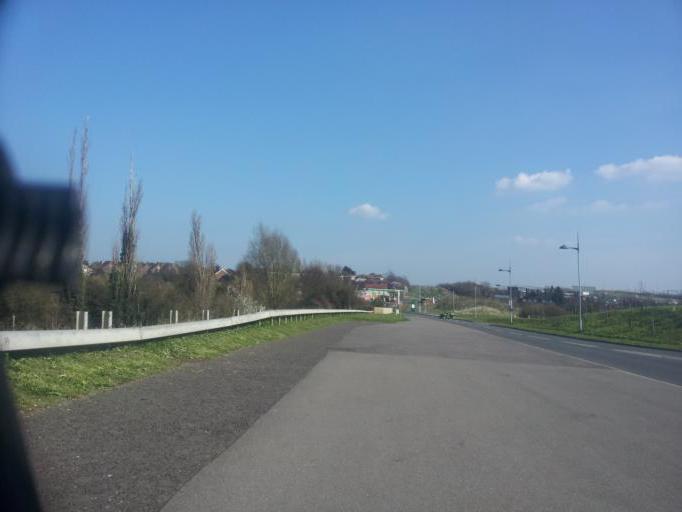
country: GB
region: England
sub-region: Kent
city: Gravesend
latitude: 51.4184
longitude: 0.3572
